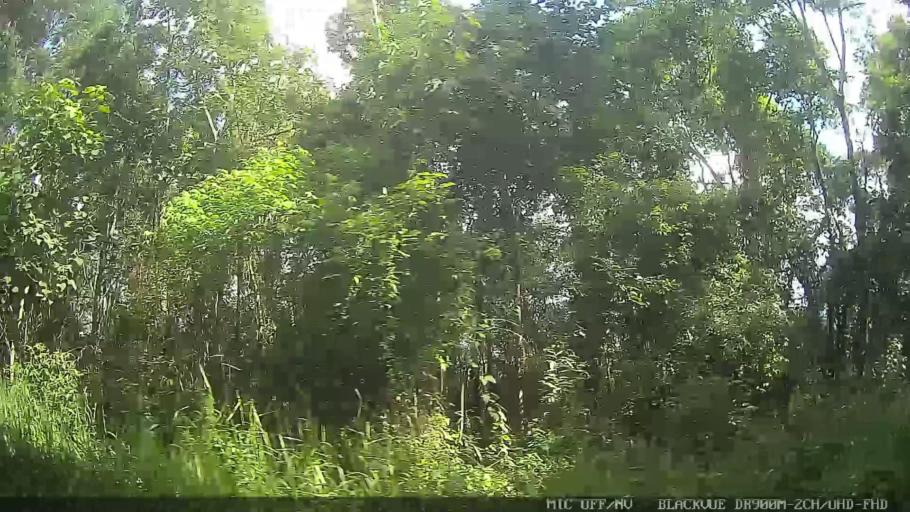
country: BR
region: Minas Gerais
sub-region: Extrema
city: Extrema
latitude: -22.8320
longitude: -46.2541
